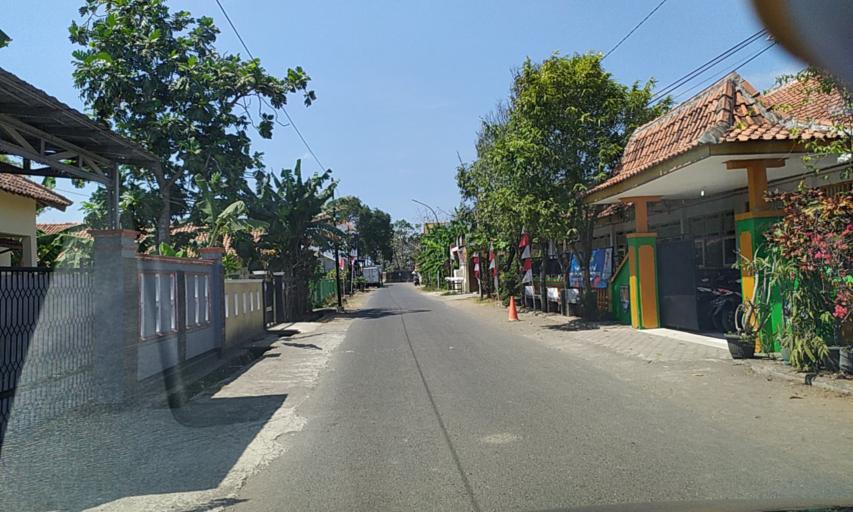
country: ID
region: Central Java
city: Rejanegara
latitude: -7.6924
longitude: 109.0511
